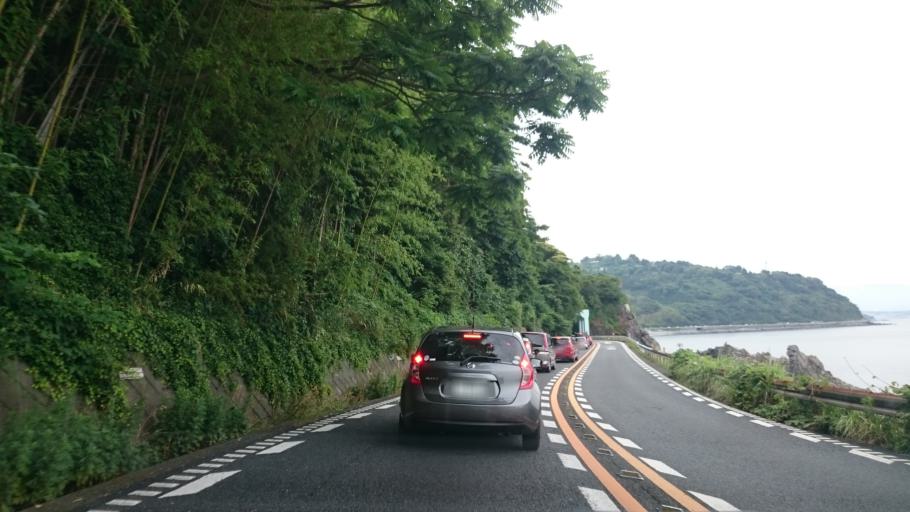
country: JP
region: Kanagawa
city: Yugawara
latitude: 35.1756
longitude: 139.1388
